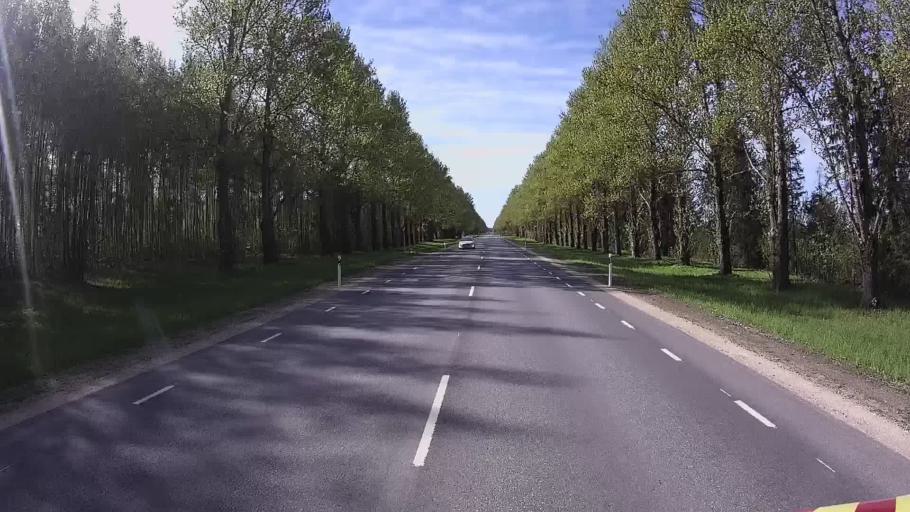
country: EE
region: Polvamaa
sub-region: Polva linn
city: Polva
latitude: 58.2974
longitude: 27.0014
